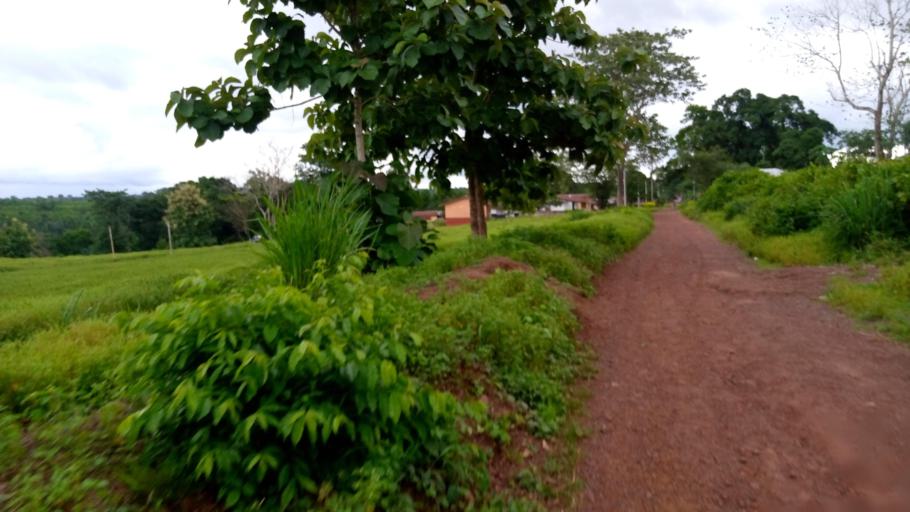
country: SL
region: Southern Province
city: Moyamba
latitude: 8.1639
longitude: -12.4423
